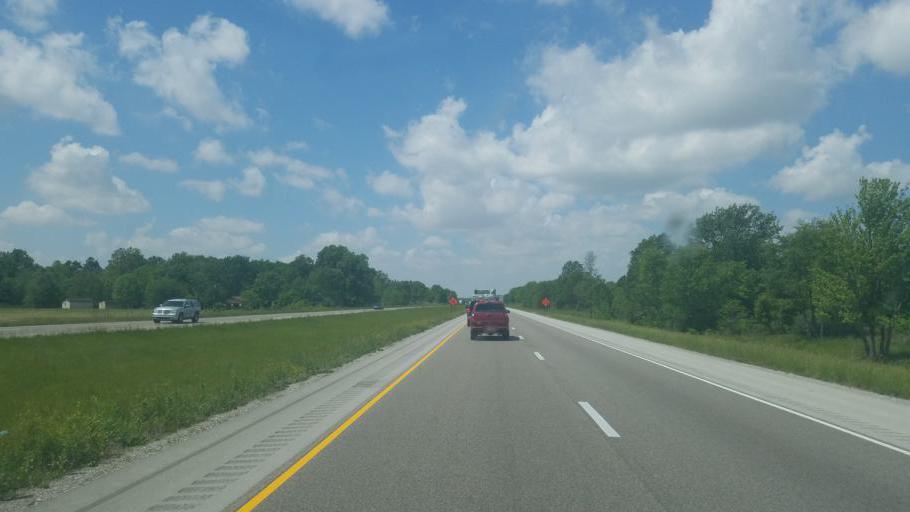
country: US
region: Illinois
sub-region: Cumberland County
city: Toledo
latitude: 39.2240
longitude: -88.2319
